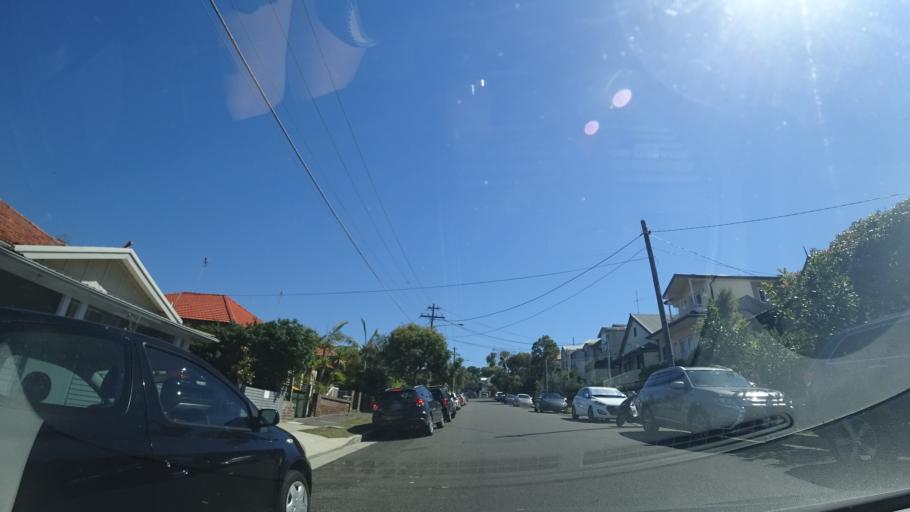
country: AU
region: New South Wales
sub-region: Randwick
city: Clovelly
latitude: -33.9112
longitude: 151.2637
